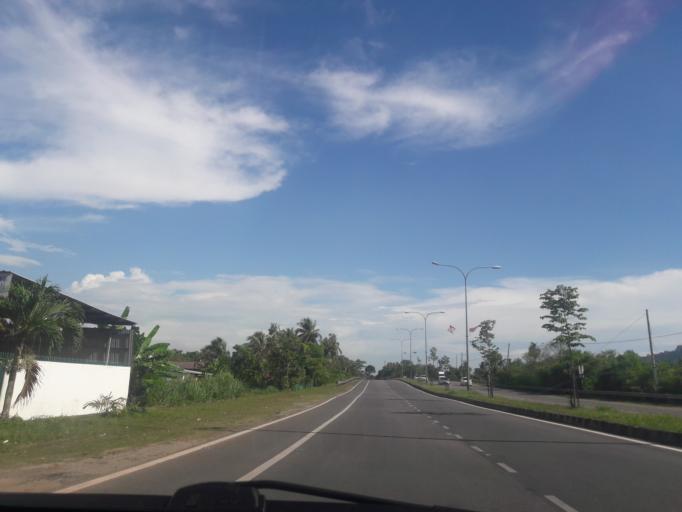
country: MY
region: Kedah
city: Sungai Petani
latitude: 5.6234
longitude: 100.4642
